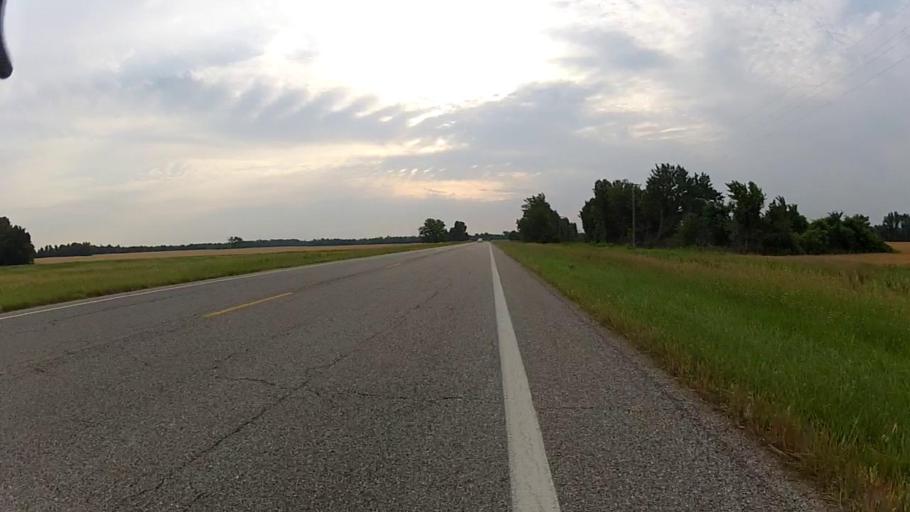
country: US
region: Kansas
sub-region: Labette County
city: Oswego
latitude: 37.1790
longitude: -94.9868
